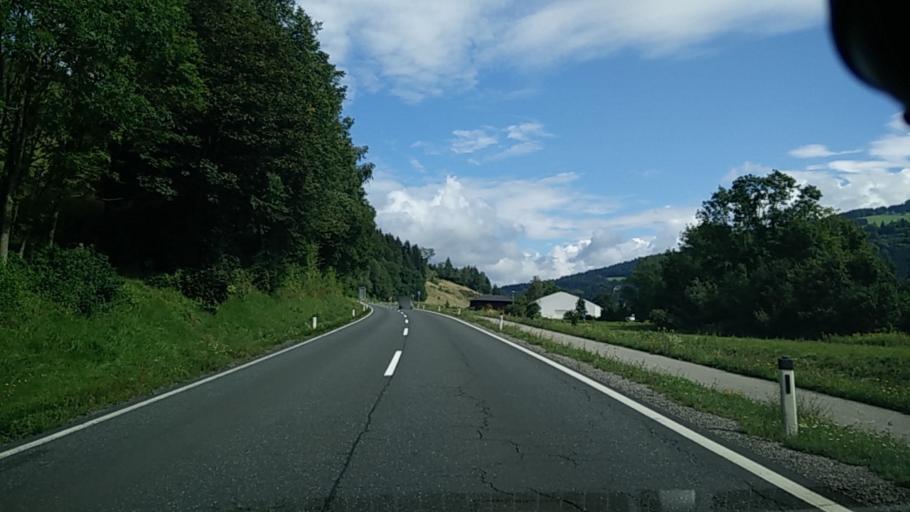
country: AT
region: Carinthia
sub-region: Politischer Bezirk Sankt Veit an der Glan
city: Bruckl
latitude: 46.7359
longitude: 14.5278
